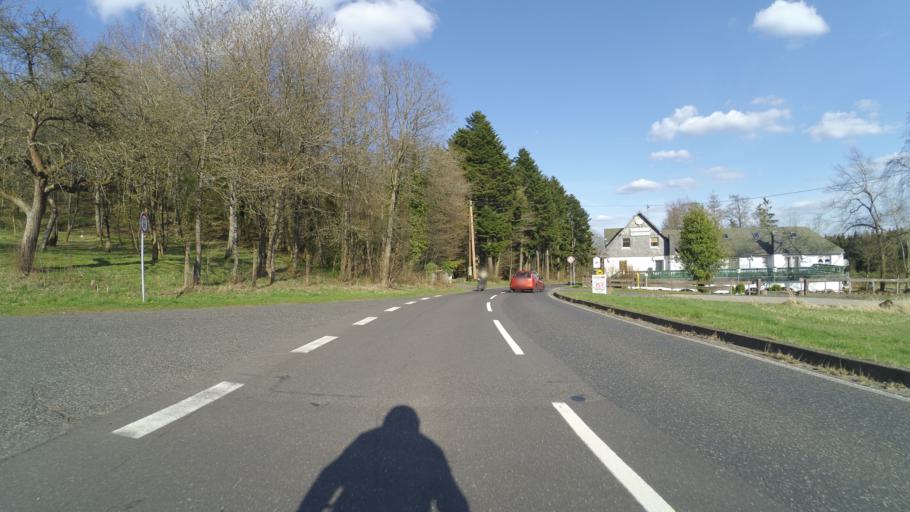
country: DE
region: Rheinland-Pfalz
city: Meuspath
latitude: 50.3465
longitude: 6.9595
